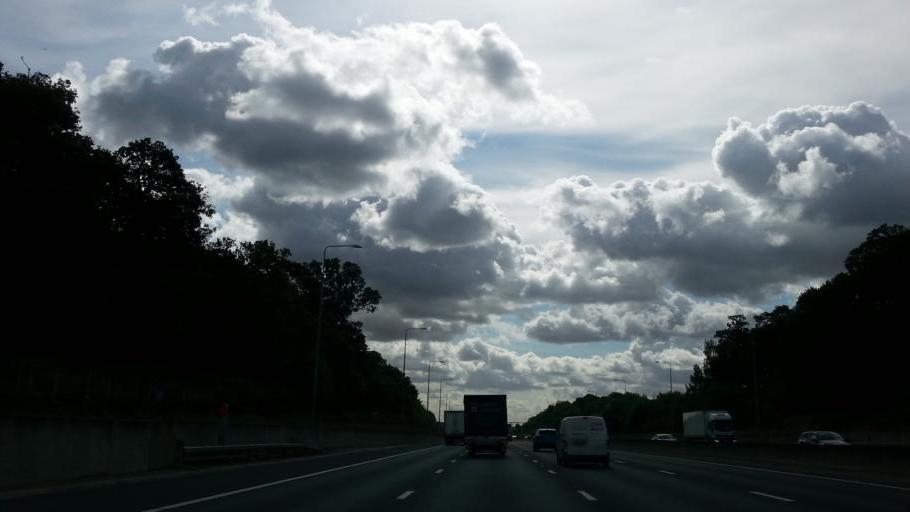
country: GB
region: England
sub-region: Greater London
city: Harold Wood
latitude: 51.6317
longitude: 0.2238
